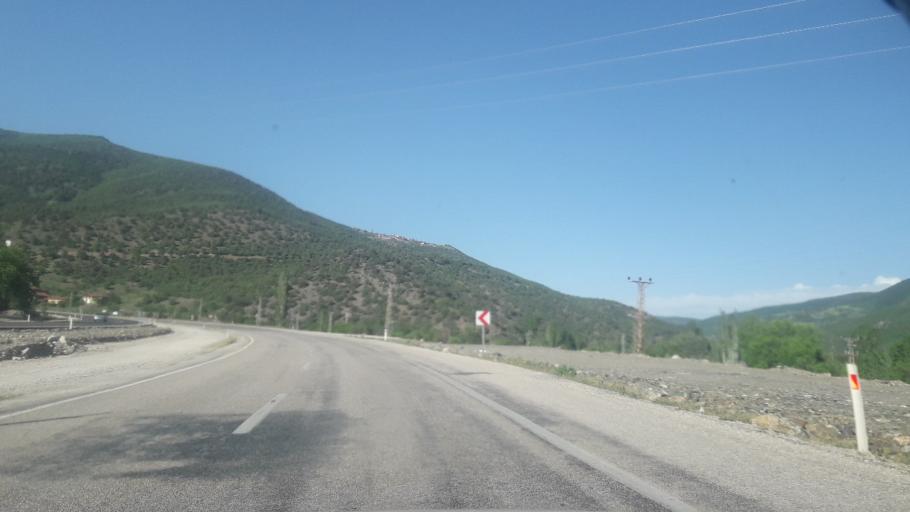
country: TR
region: Tokat
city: Turhal
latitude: 40.4784
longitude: 36.1545
